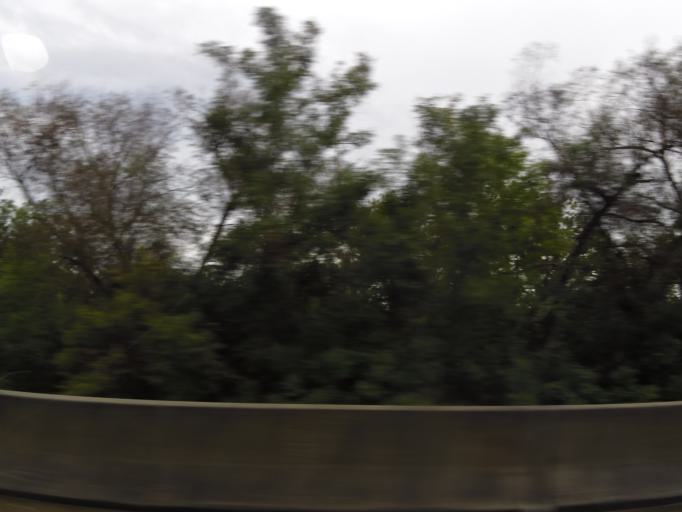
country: US
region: Georgia
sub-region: Wayne County
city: Jesup
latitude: 31.6736
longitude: -81.8256
